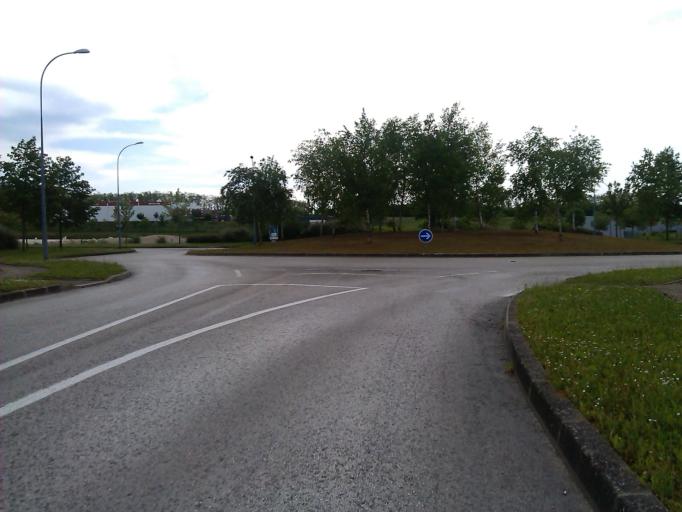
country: FR
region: Franche-Comte
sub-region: Departement du Jura
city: Dole
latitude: 47.1067
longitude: 5.5033
